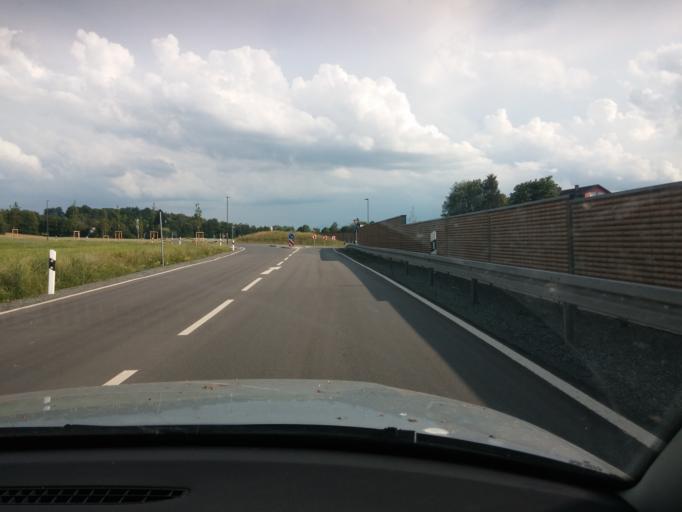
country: DE
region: Bavaria
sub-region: Upper Bavaria
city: Grafing bei Munchen
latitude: 48.0477
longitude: 11.9750
